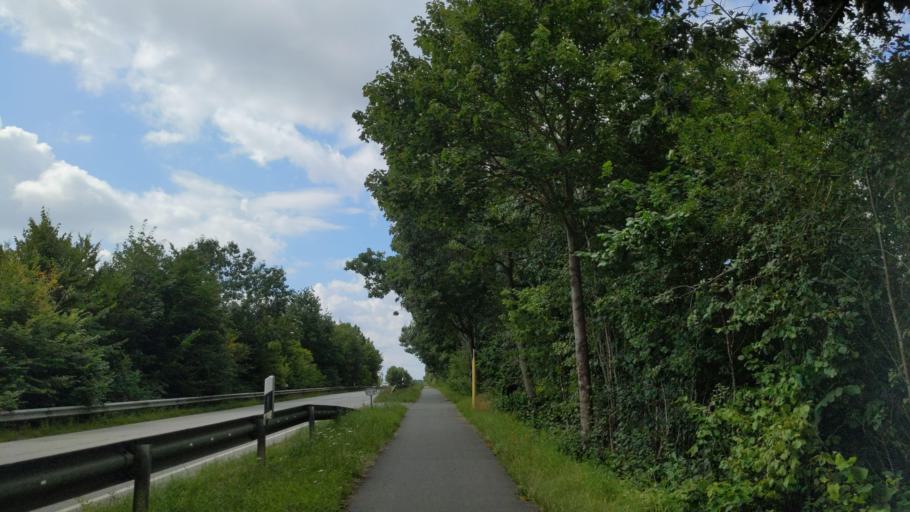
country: DE
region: Schleswig-Holstein
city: Hamberge
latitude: 53.8381
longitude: 10.5694
